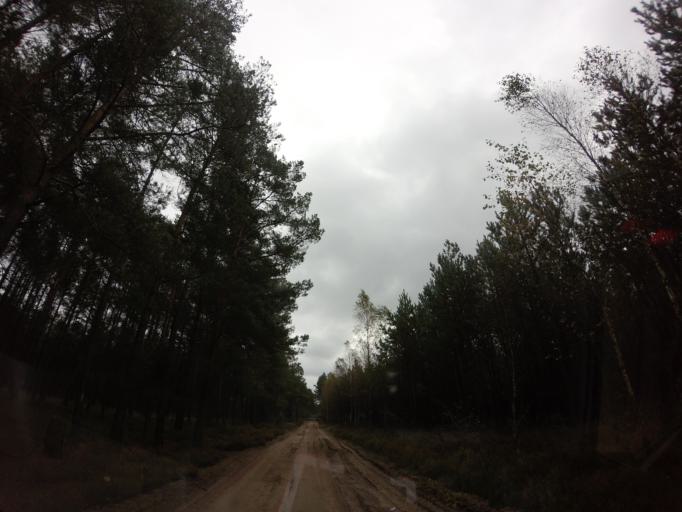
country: PL
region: West Pomeranian Voivodeship
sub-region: Powiat choszczenski
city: Drawno
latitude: 53.1349
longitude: 15.7636
